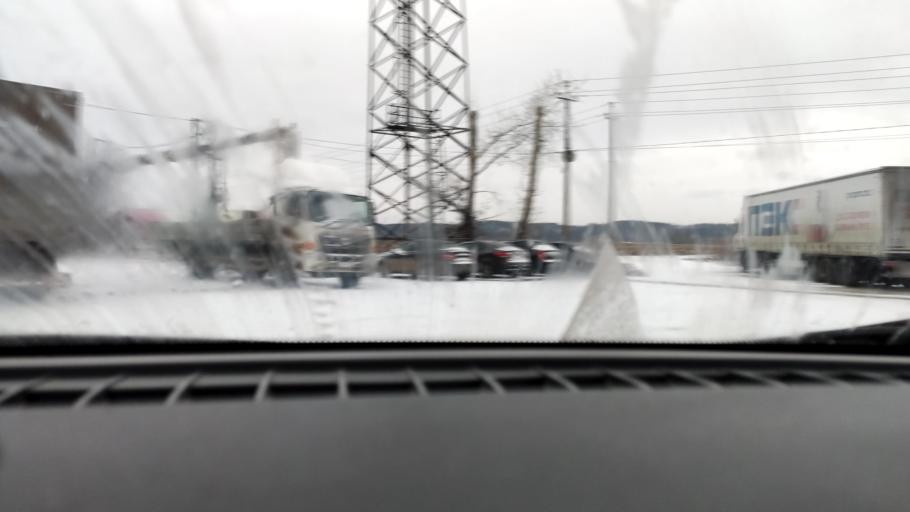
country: RU
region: Perm
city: Kondratovo
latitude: 57.9235
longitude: 56.1667
